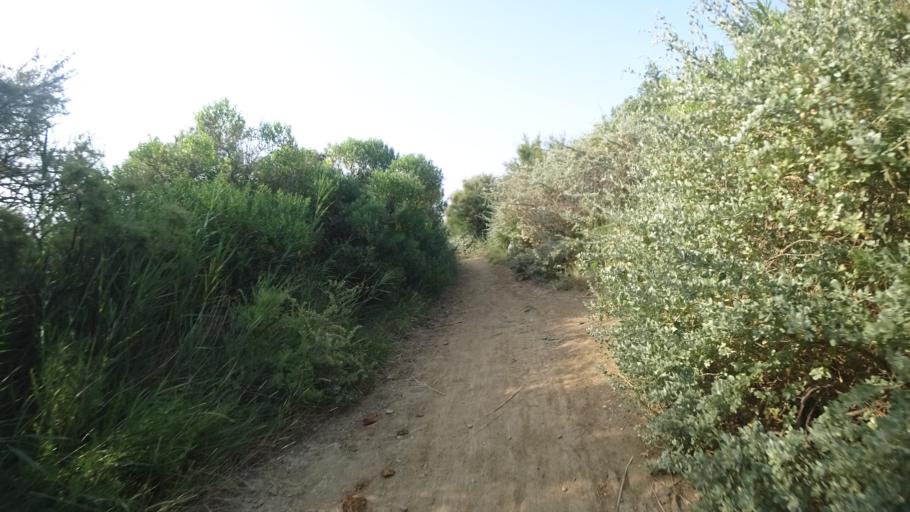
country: FR
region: Languedoc-Roussillon
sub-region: Departement des Pyrenees-Orientales
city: Sainte-Marie-Plage
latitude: 42.7425
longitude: 3.0365
